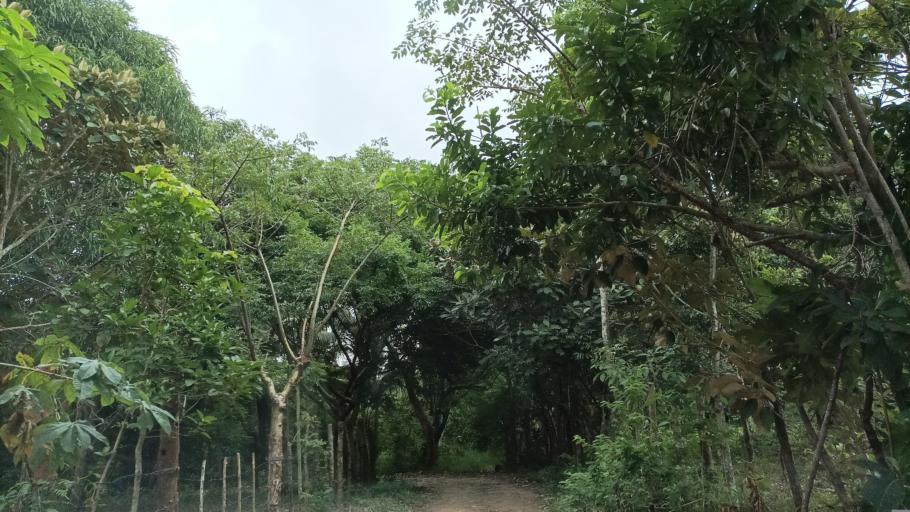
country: MX
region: Veracruz
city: Minatitlan
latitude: 18.0427
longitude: -94.5570
